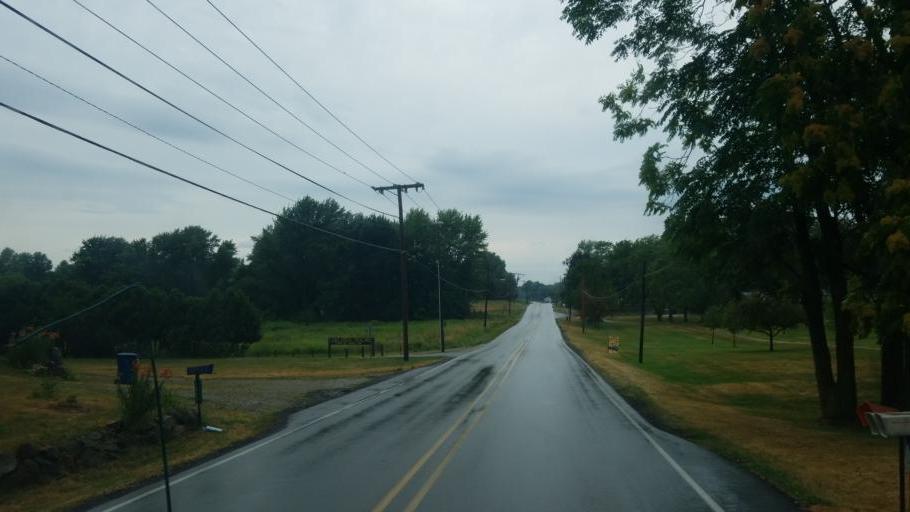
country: US
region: Indiana
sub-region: Steuben County
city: Hamilton
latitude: 41.5348
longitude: -84.9186
